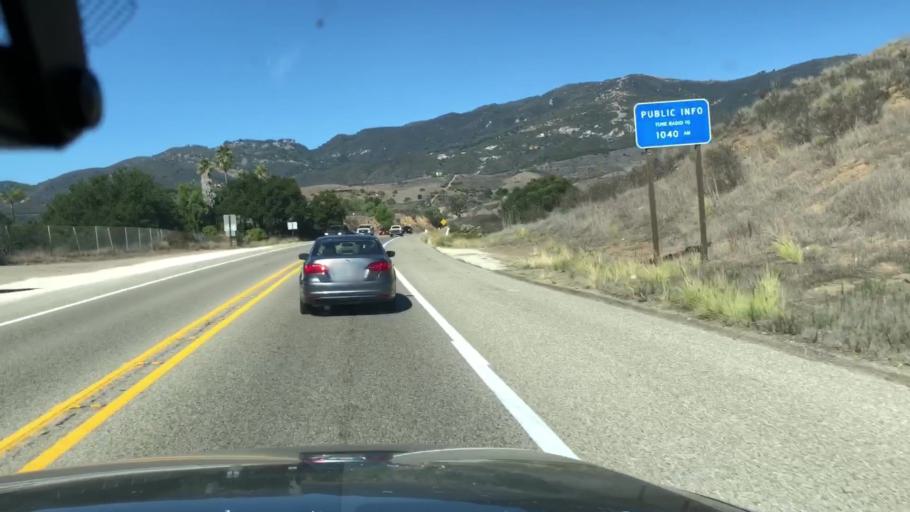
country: US
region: California
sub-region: Santa Barbara County
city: Mission Canyon
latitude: 34.4627
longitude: -119.7711
